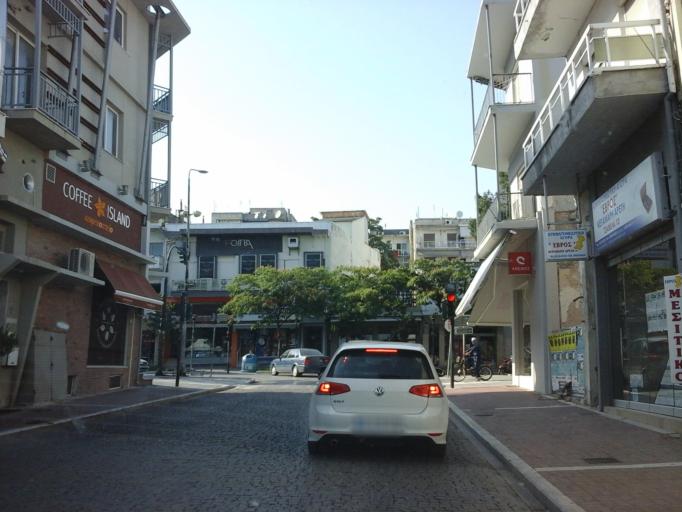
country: GR
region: East Macedonia and Thrace
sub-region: Nomos Evrou
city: Alexandroupoli
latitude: 40.8459
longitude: 25.8778
